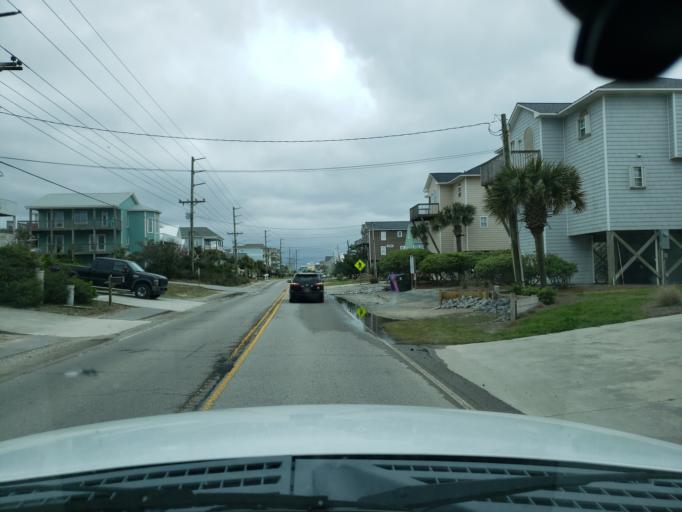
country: US
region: North Carolina
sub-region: Pender County
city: Surf City
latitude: 34.4104
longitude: -77.5693
